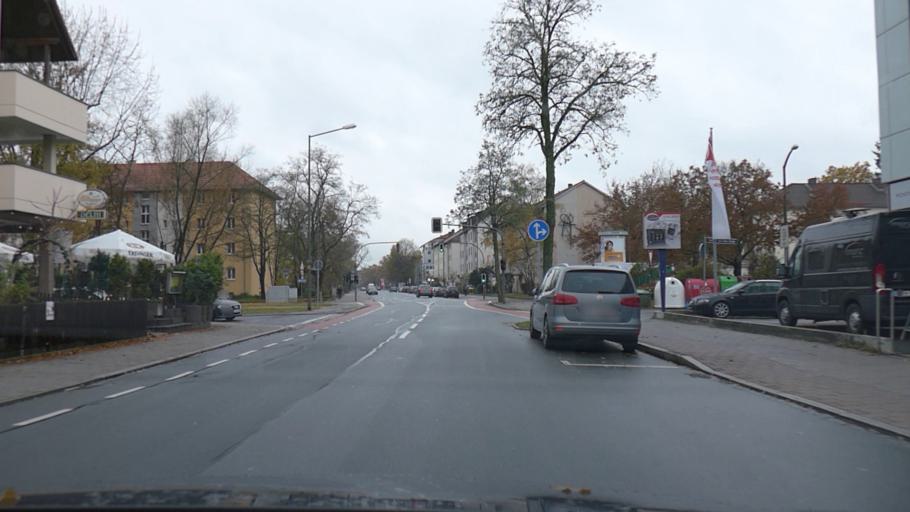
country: DE
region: Bavaria
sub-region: Regierungsbezirk Mittelfranken
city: Erlangen
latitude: 49.5918
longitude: 11.0173
